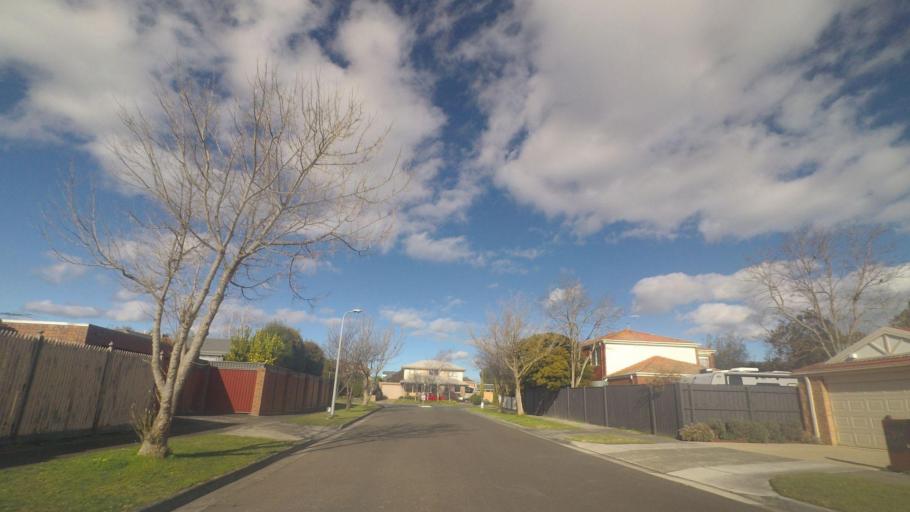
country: AU
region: Victoria
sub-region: Yarra Ranges
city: Lysterfield
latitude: -37.9147
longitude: 145.2799
